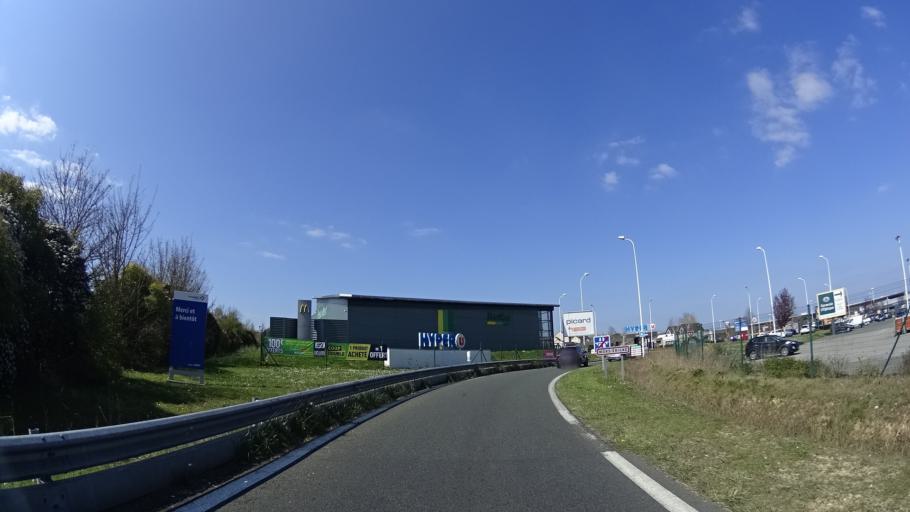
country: FR
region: Pays de la Loire
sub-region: Departement de Maine-et-Loire
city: Murs-Erigne
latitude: 47.3958
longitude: -0.5279
